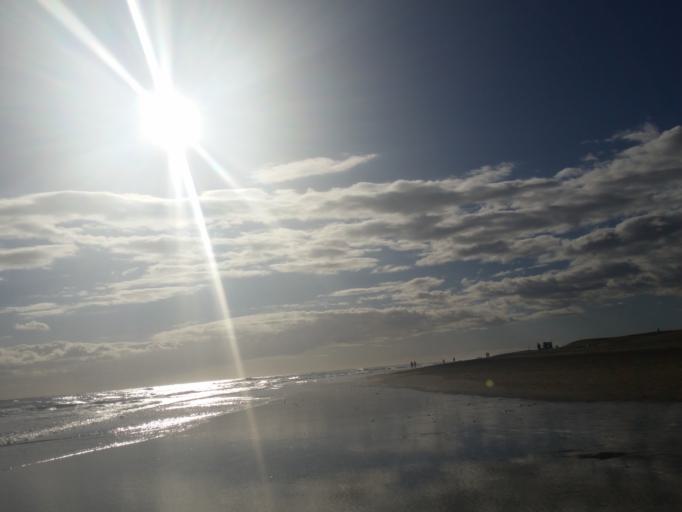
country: ES
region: Canary Islands
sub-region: Provincia de Las Palmas
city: Playa del Ingles
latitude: 27.7383
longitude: -15.5685
